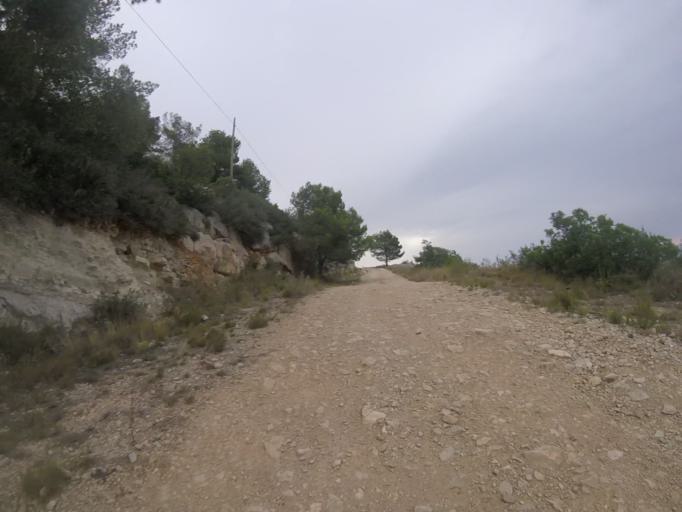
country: ES
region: Valencia
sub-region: Provincia de Castello
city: Alcoceber
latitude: 40.2774
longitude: 0.2819
